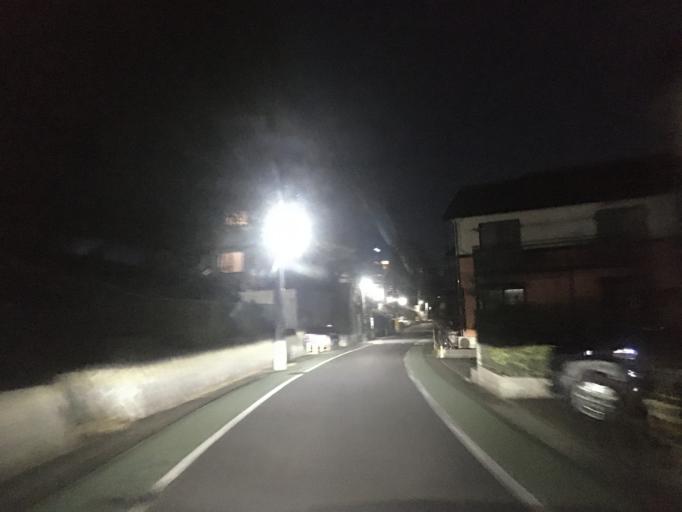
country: JP
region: Tokyo
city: Chofugaoka
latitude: 35.6052
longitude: 139.5209
